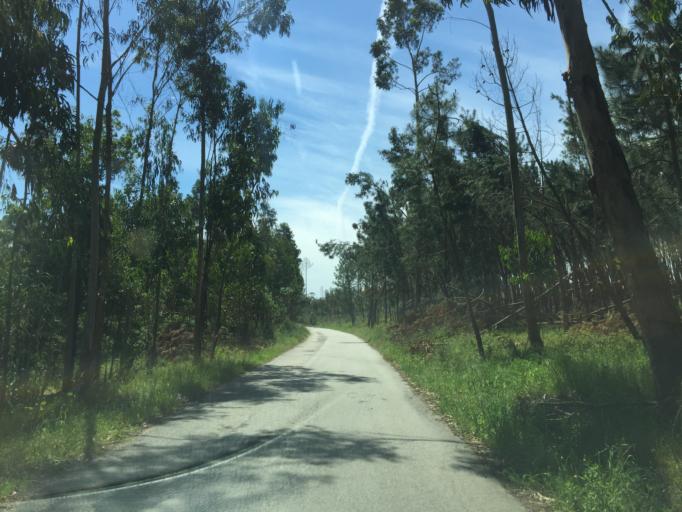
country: PT
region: Coimbra
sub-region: Figueira da Foz
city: Lavos
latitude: 40.0799
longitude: -8.7778
